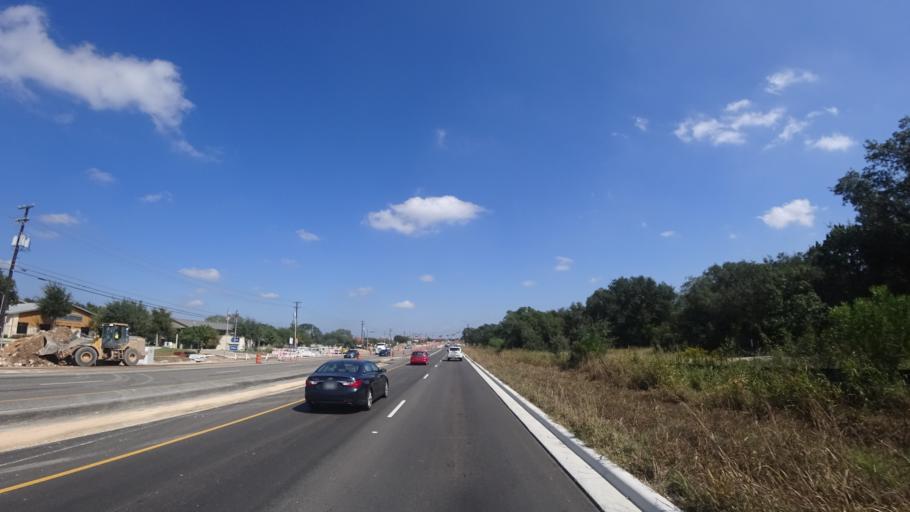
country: US
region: Texas
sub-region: Williamson County
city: Round Rock
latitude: 30.5105
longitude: -97.7086
